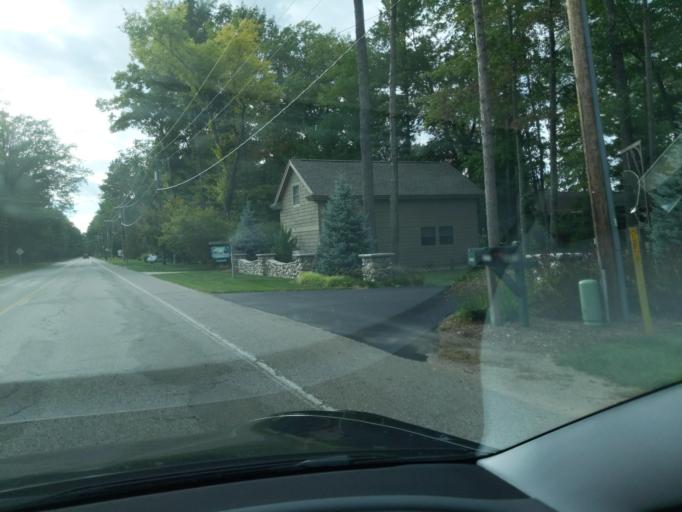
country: US
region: Michigan
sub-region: Kalkaska County
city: Rapid City
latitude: 44.8537
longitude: -85.3093
